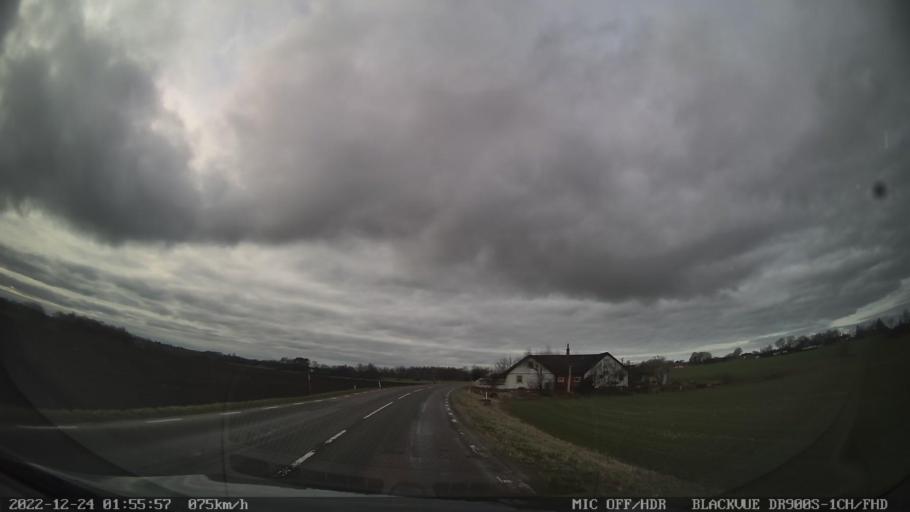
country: SE
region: Skane
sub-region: Tomelilla Kommun
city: Tomelilla
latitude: 55.5995
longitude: 14.0663
